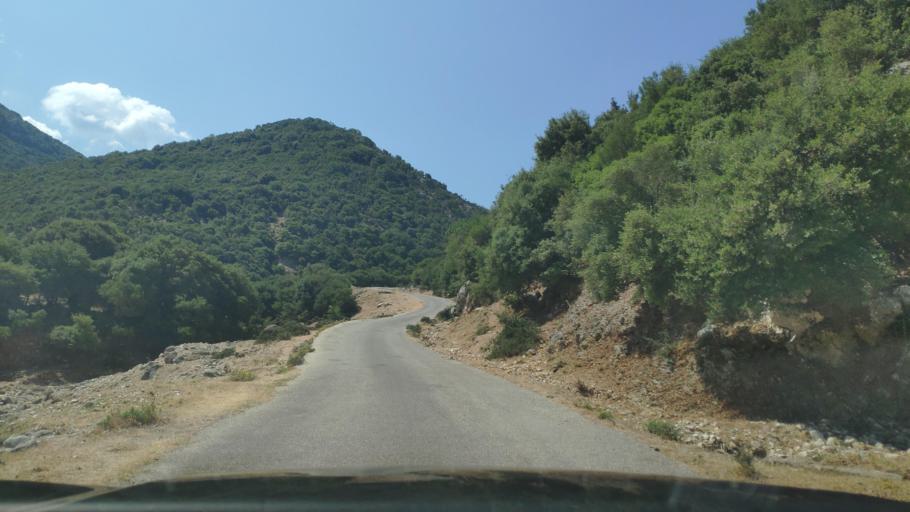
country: GR
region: West Greece
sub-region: Nomos Aitolias kai Akarnanias
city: Monastirakion
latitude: 38.8344
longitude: 20.9326
